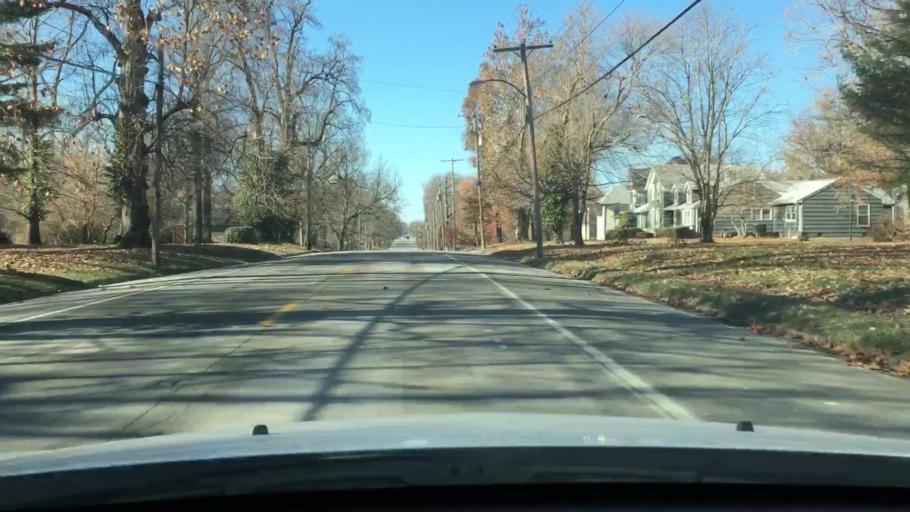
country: US
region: Illinois
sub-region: Pike County
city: Pittsfield
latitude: 39.6068
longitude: -90.7936
